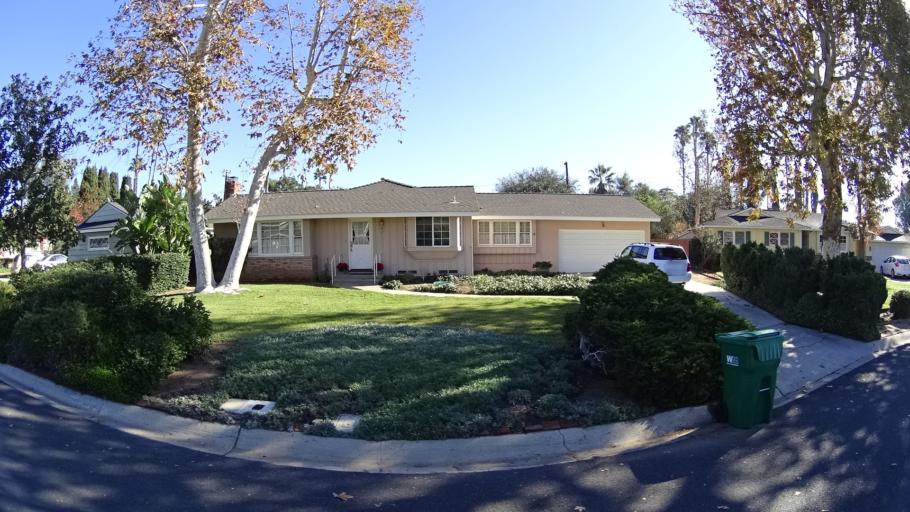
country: US
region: California
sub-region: Orange County
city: North Tustin
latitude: 33.7651
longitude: -117.8083
